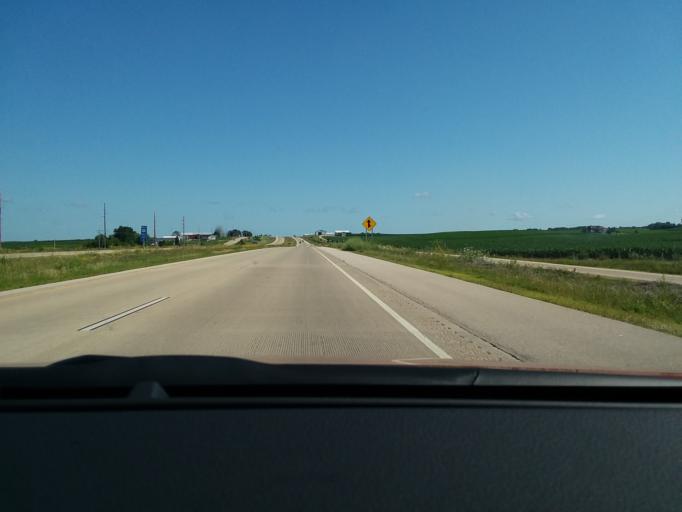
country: US
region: Wisconsin
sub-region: Dane County
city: Windsor
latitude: 43.2185
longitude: -89.3227
